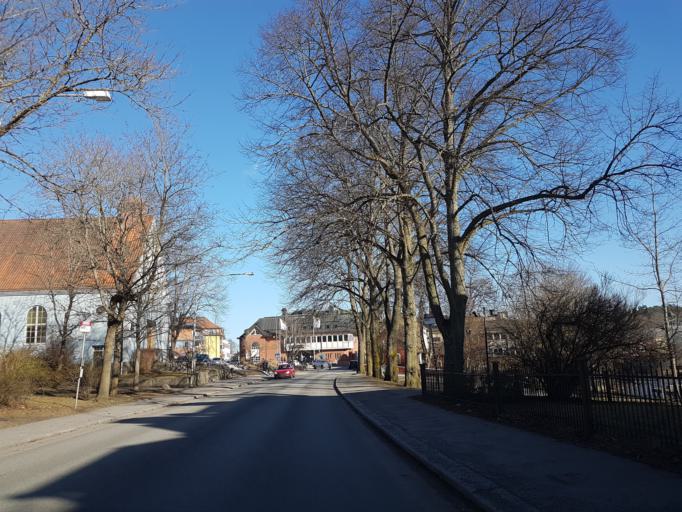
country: SE
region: Stockholm
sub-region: Norrtalje Kommun
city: Norrtalje
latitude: 59.7587
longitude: 18.6998
